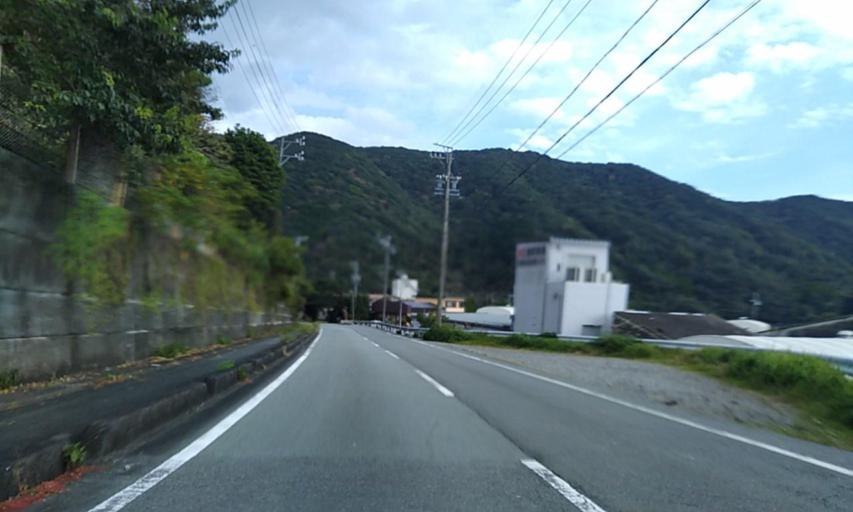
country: JP
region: Mie
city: Ise
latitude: 34.2792
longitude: 136.5096
